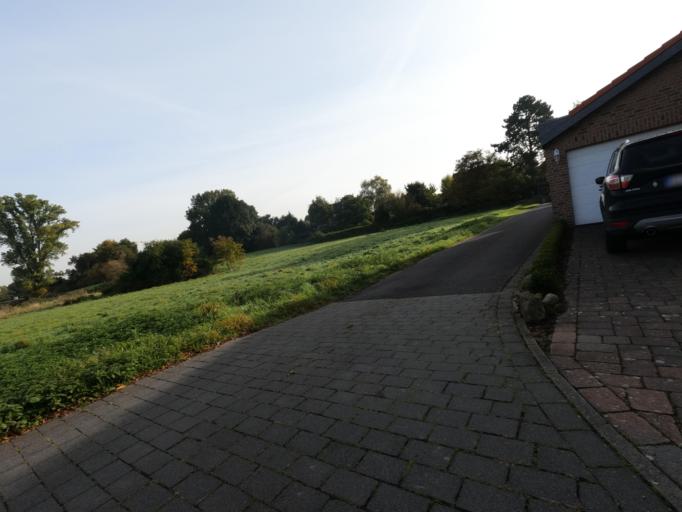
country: DE
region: North Rhine-Westphalia
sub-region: Regierungsbezirk Koln
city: Linnich
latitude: 50.9802
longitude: 6.2614
